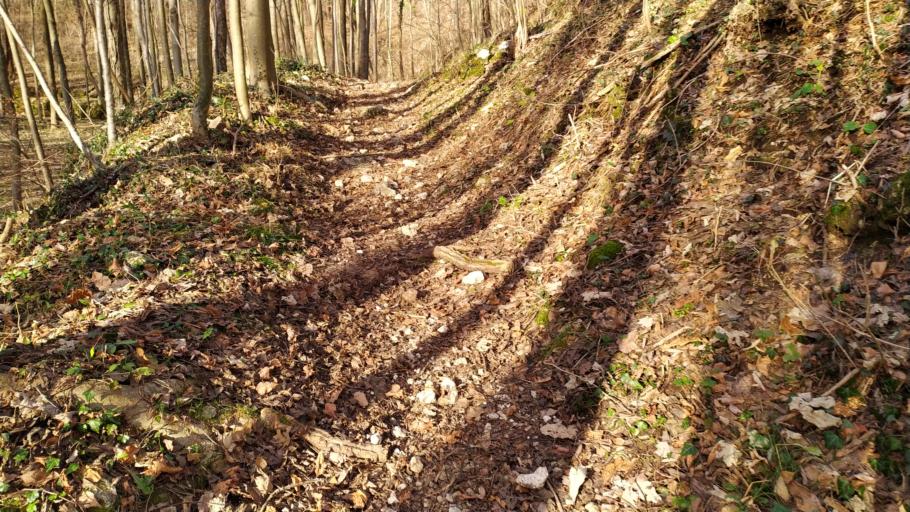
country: IT
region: Veneto
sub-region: Provincia di Vicenza
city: Velo d'Astico
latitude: 45.7640
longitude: 11.3578
